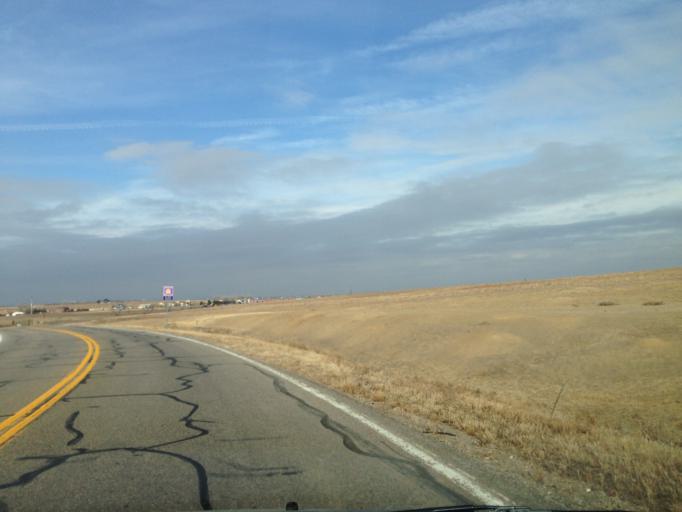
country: US
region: Colorado
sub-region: Boulder County
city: Lafayette
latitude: 40.0007
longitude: -105.0530
